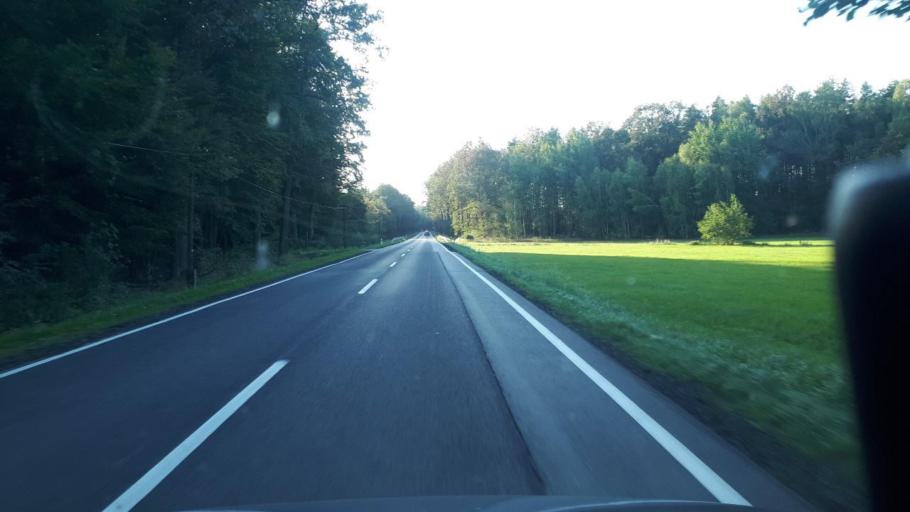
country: PL
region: Opole Voivodeship
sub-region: Powiat oleski
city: Olesno
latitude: 50.8475
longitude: 18.4793
